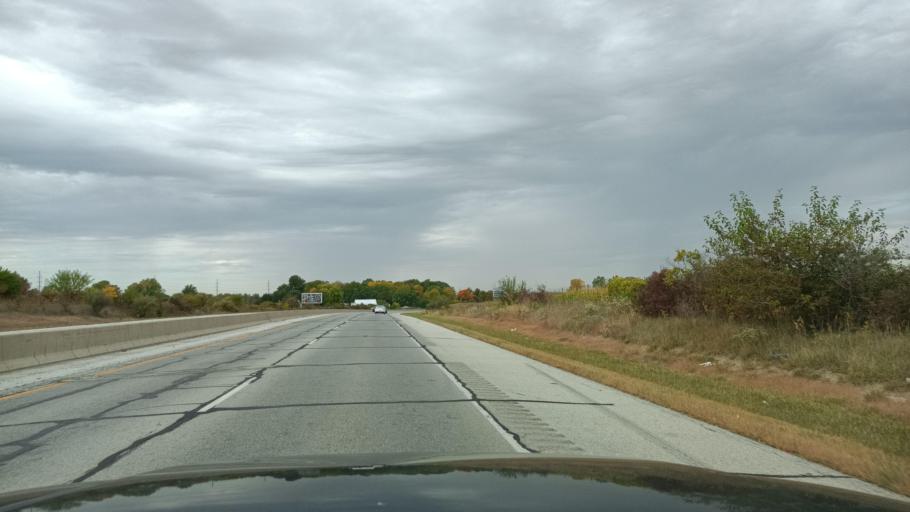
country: US
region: Indiana
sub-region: Delaware County
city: Yorktown
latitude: 40.2192
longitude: -85.5121
